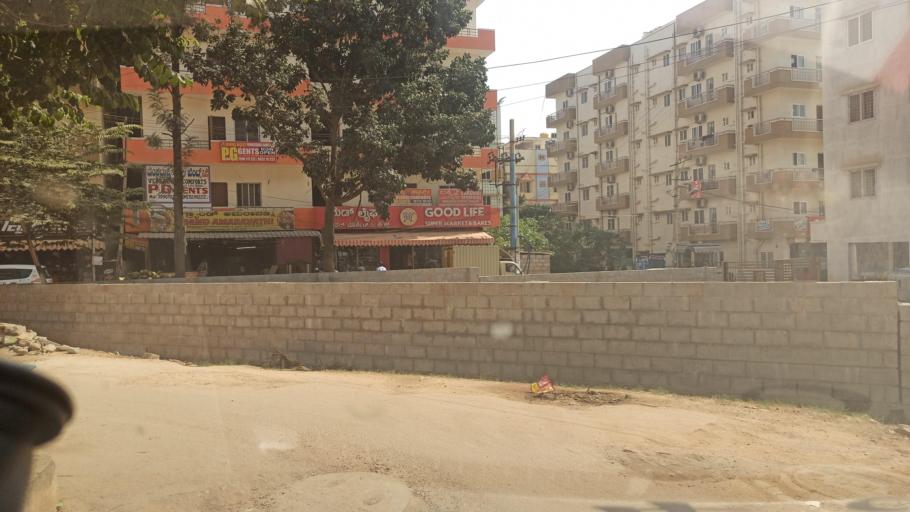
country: IN
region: Karnataka
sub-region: Bangalore Urban
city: Bangalore
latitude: 12.9517
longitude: 77.7038
